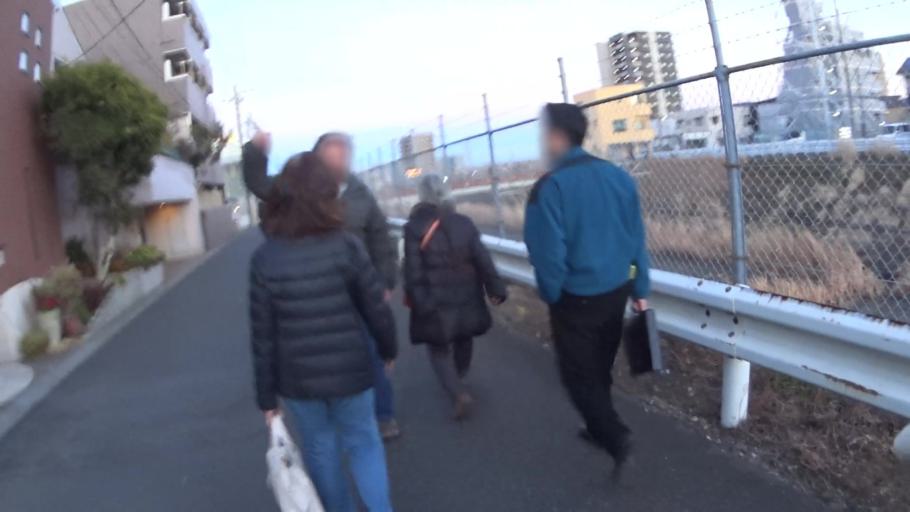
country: JP
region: Saitama
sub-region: Kawaguchi-shi
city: Hatogaya-honcho
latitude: 35.8746
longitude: 139.7425
